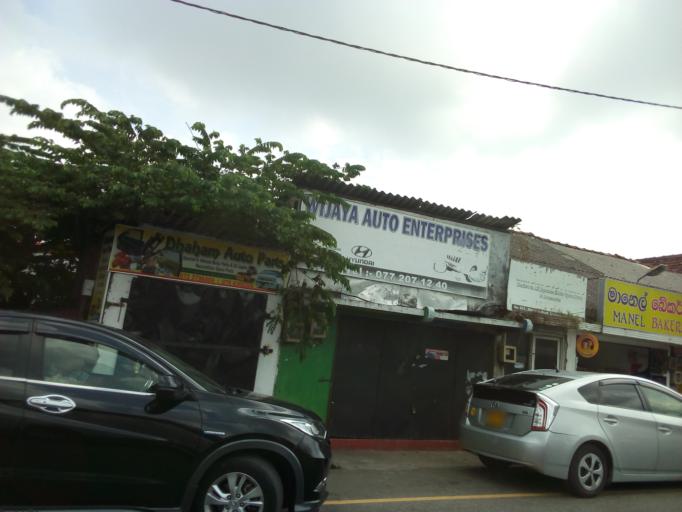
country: LK
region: Western
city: Sri Jayewardenepura Kotte
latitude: 6.8600
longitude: 79.9062
